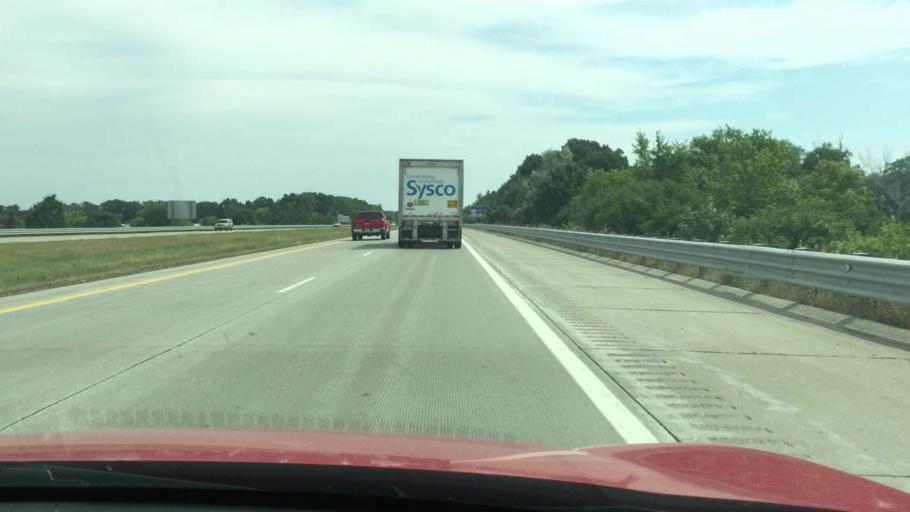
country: US
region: Michigan
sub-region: Genesee County
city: Flint
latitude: 42.9579
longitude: -83.6827
